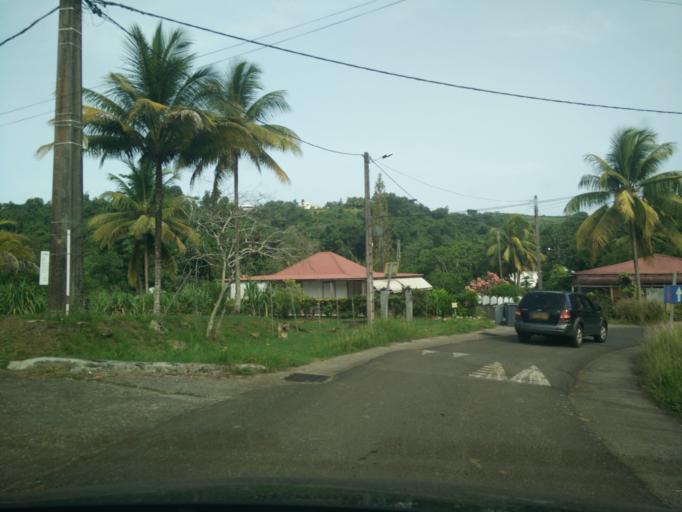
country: GP
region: Guadeloupe
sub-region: Guadeloupe
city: Petit-Bourg
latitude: 16.1189
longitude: -61.5946
